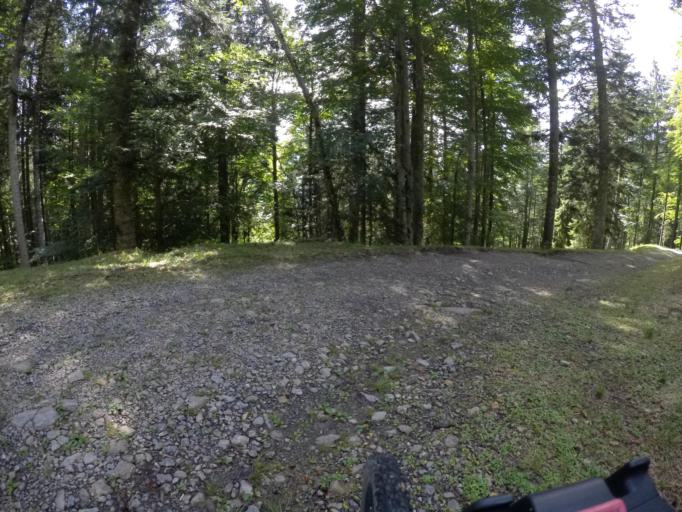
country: IT
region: Friuli Venezia Giulia
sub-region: Provincia di Udine
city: Paularo
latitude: 46.5061
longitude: 13.1763
